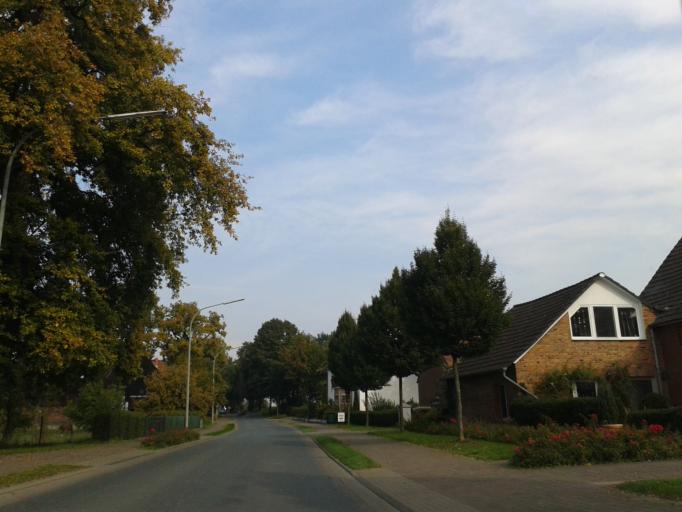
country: DE
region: North Rhine-Westphalia
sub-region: Regierungsbezirk Detmold
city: Salzkotten
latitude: 51.7176
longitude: 8.6267
